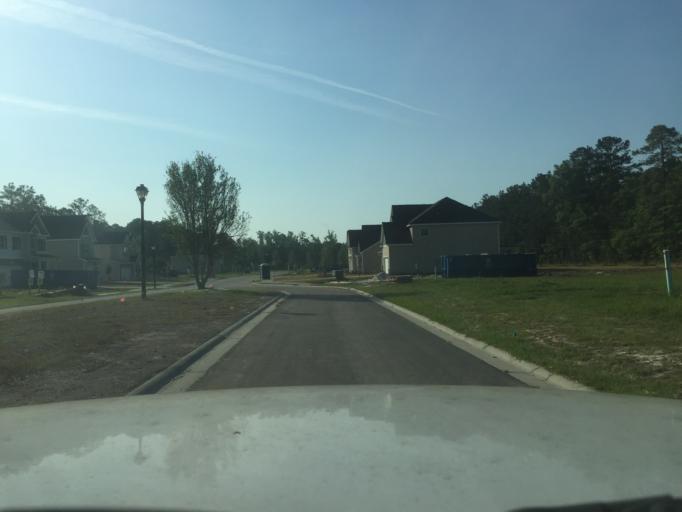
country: US
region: Georgia
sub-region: Chatham County
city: Georgetown
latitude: 32.0384
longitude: -81.2223
